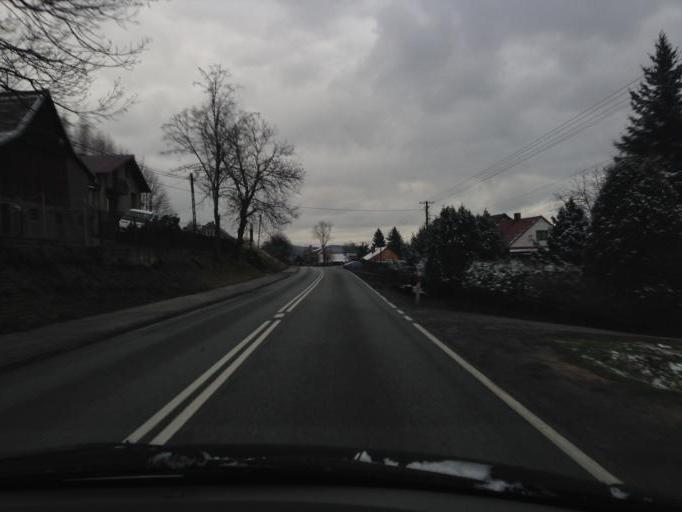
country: PL
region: Lesser Poland Voivodeship
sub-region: Powiat brzeski
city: Zlota
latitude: 49.8613
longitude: 20.7169
